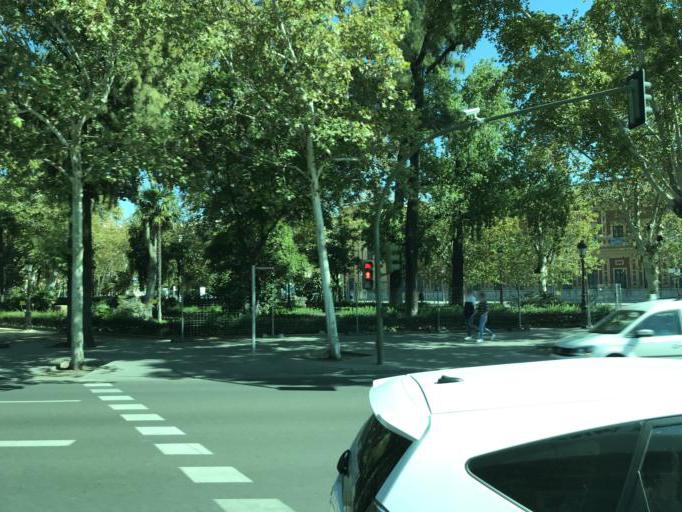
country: ES
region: Andalusia
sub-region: Provincia de Sevilla
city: Sevilla
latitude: 37.3805
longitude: -5.9946
